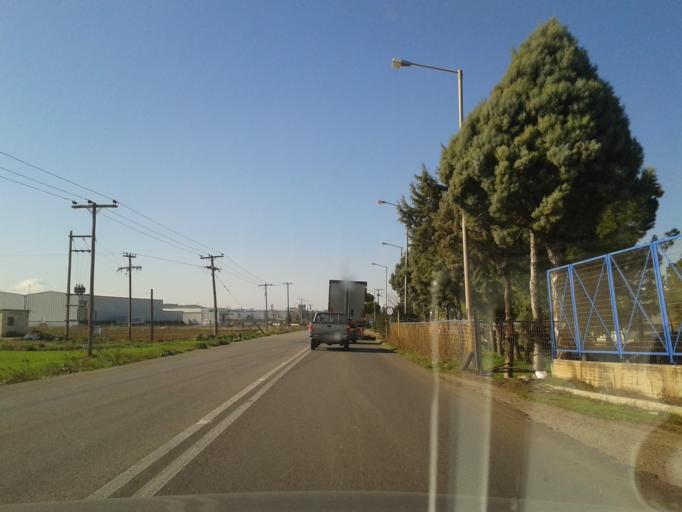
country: GR
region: Central Greece
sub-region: Nomos Voiotias
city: Thivai
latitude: 38.3534
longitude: 23.3902
